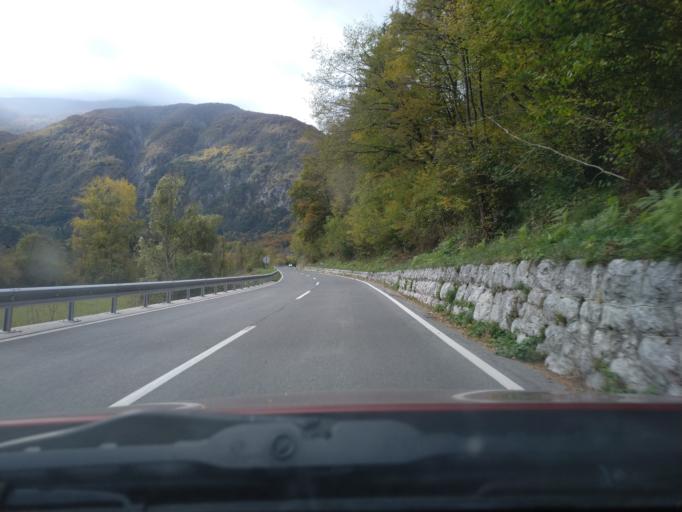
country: SI
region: Bovec
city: Bovec
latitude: 46.3128
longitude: 13.4854
